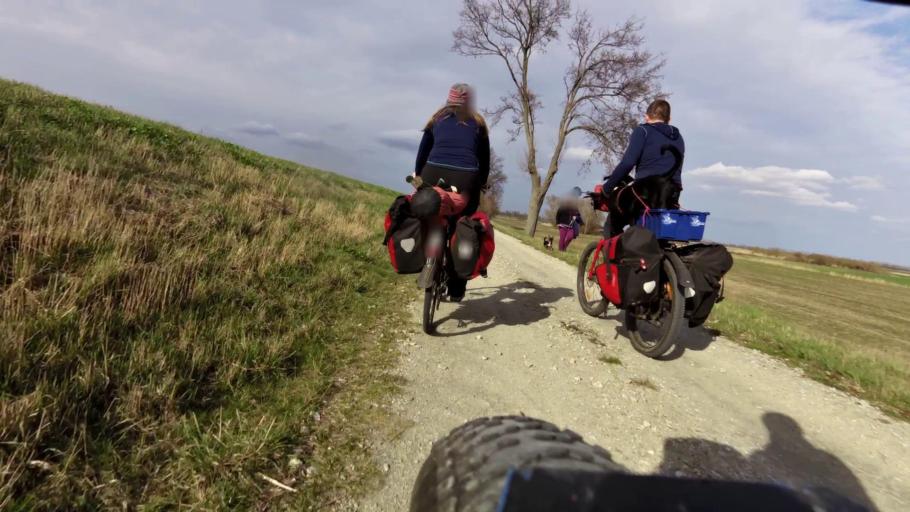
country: PL
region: Lubusz
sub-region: Powiat gorzowski
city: Kostrzyn nad Odra
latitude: 52.5474
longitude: 14.6200
